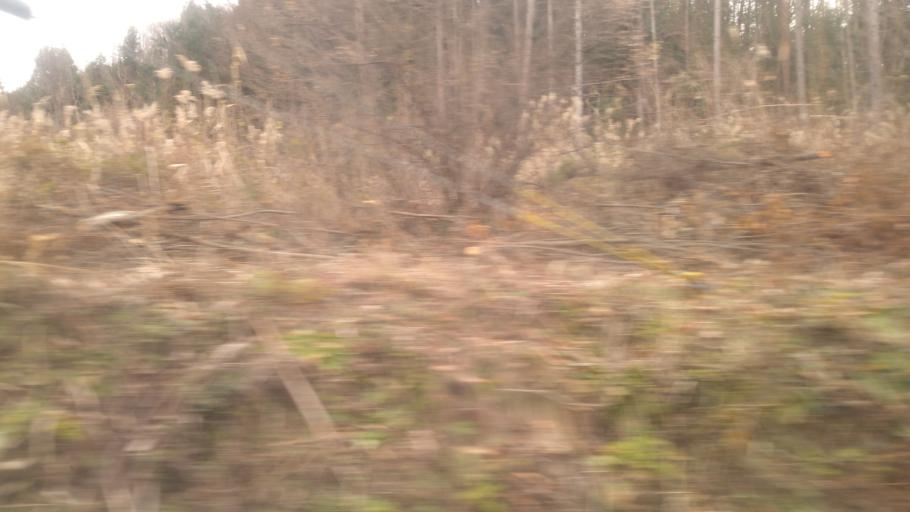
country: JP
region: Nagano
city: Hotaka
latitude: 36.4340
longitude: 138.0200
